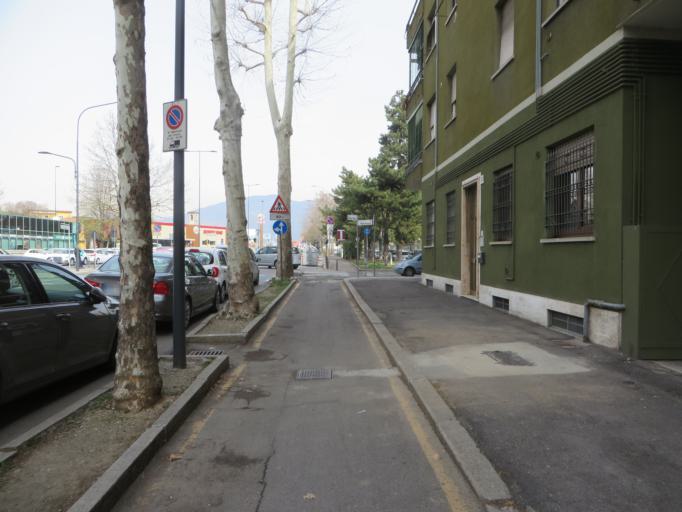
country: IT
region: Lombardy
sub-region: Provincia di Brescia
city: Brescia
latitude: 45.5570
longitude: 10.2279
